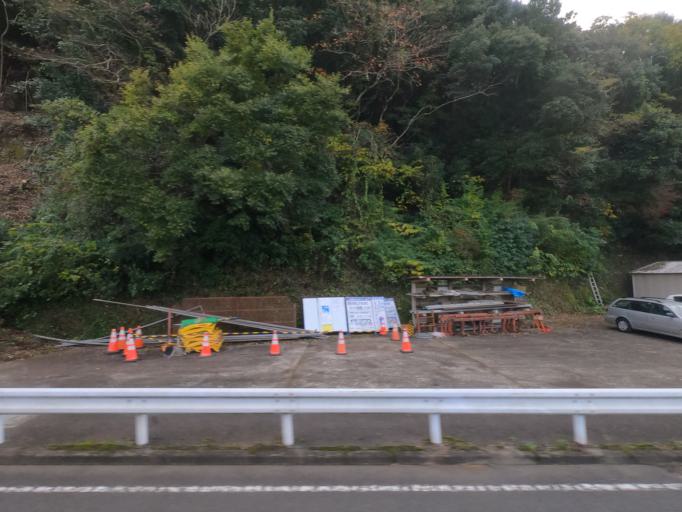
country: JP
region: Kumamoto
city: Minamata
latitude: 32.2668
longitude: 130.5062
